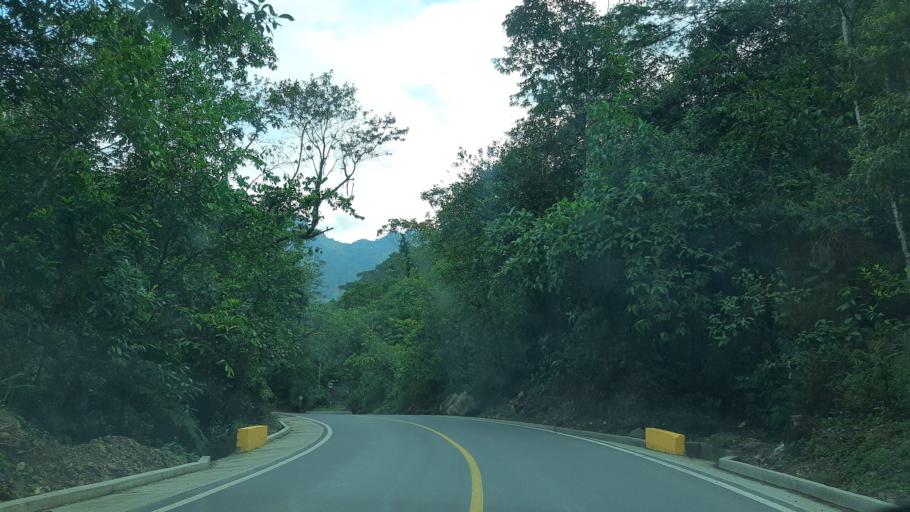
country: CO
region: Boyaca
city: Santa Maria
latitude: 4.8666
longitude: -73.2322
